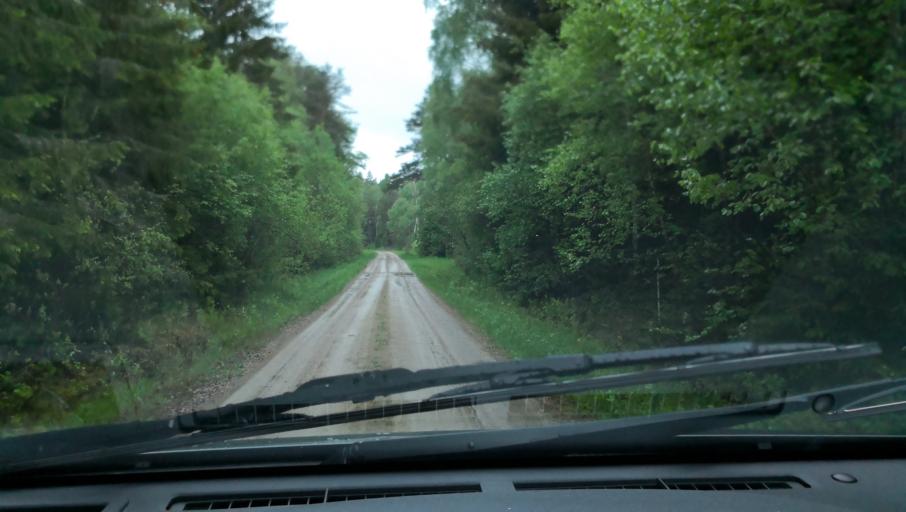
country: SE
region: Uppsala
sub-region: Enkopings Kommun
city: Orsundsbro
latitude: 59.9254
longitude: 17.3376
